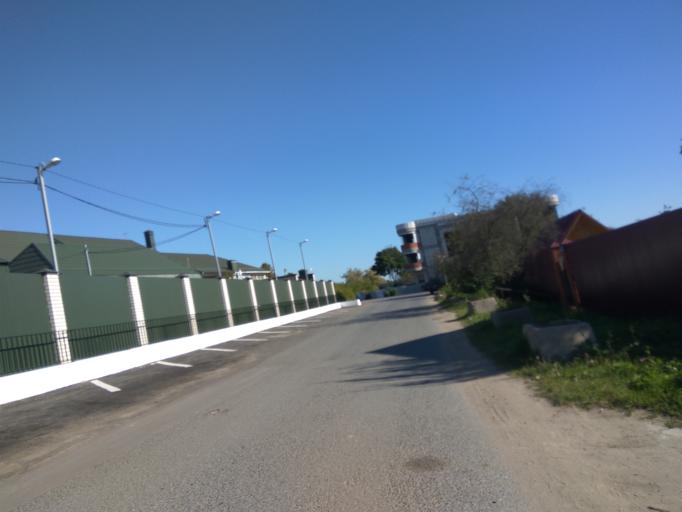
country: RU
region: Moskovskaya
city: Rechitsy
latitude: 55.6083
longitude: 38.4444
